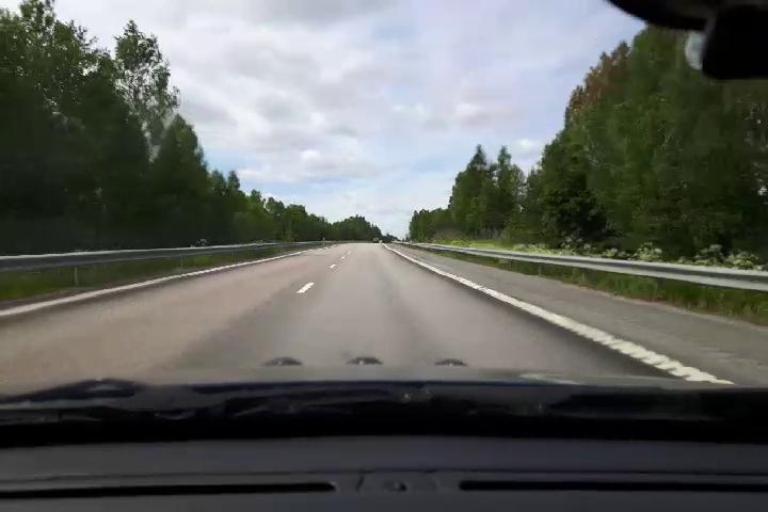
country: SE
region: Uppsala
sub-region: Alvkarleby Kommun
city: AElvkarleby
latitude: 60.4770
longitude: 17.3747
